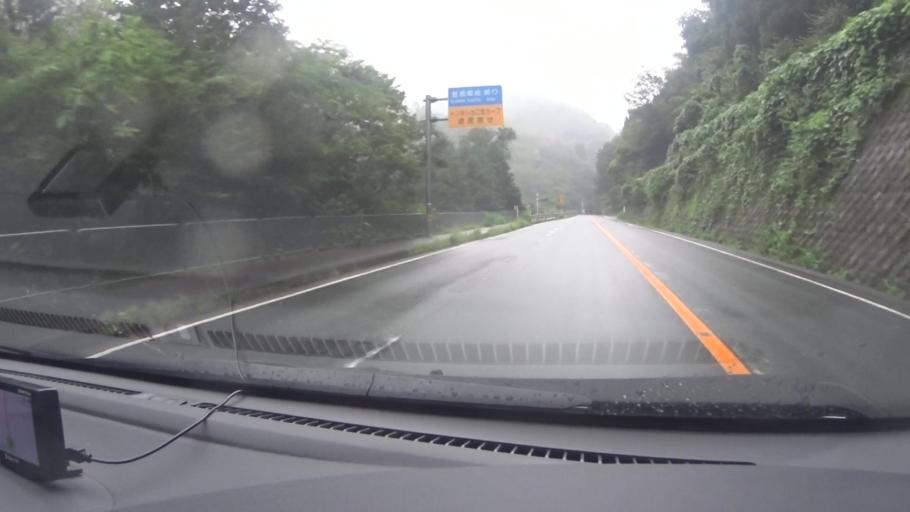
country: JP
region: Kyoto
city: Ayabe
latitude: 35.2430
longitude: 135.3127
